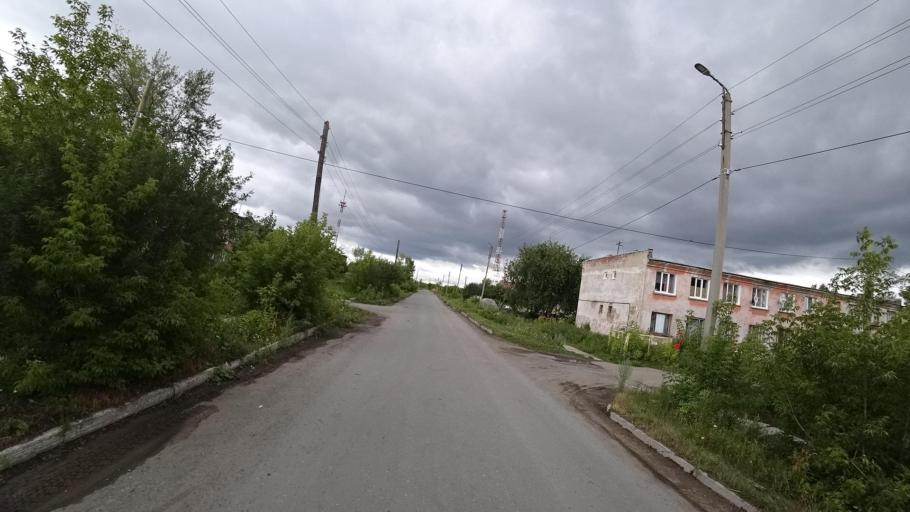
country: RU
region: Sverdlovsk
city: Kamyshlov
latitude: 56.8553
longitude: 62.7303
